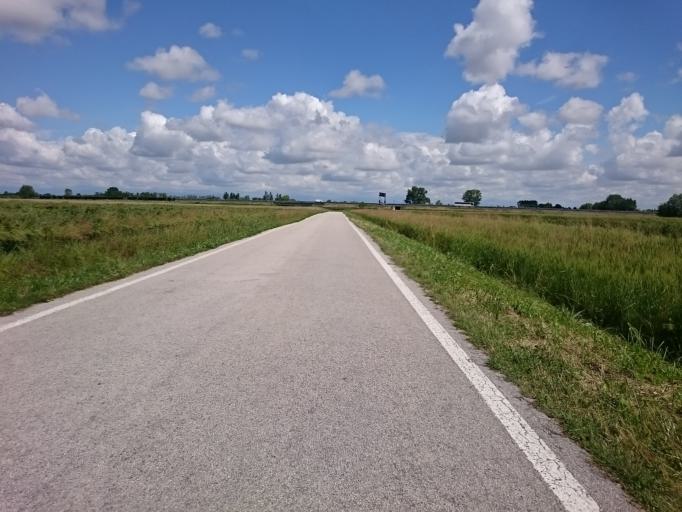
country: IT
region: Veneto
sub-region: Provincia di Padova
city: Arlesega
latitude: 45.4687
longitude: 11.7262
